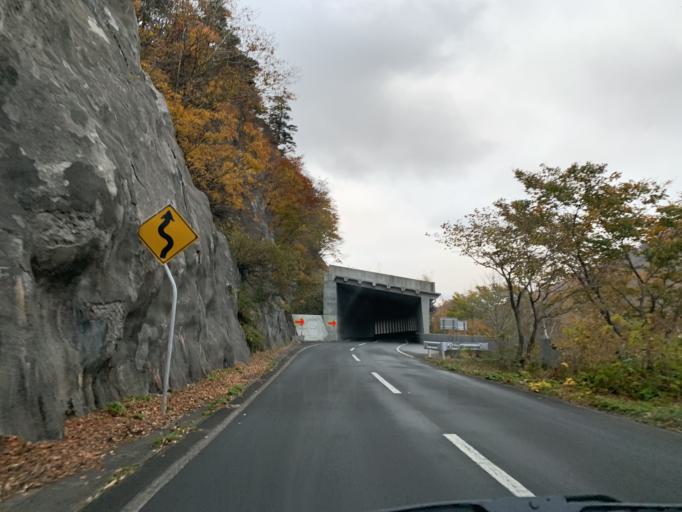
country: JP
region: Iwate
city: Mizusawa
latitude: 39.1130
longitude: 140.8459
